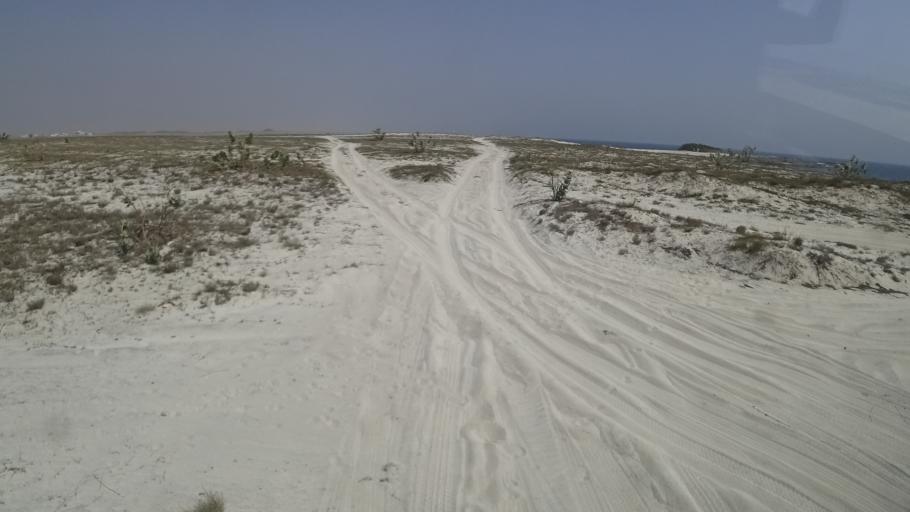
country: OM
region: Zufar
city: Salalah
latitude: 16.9703
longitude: 54.7034
